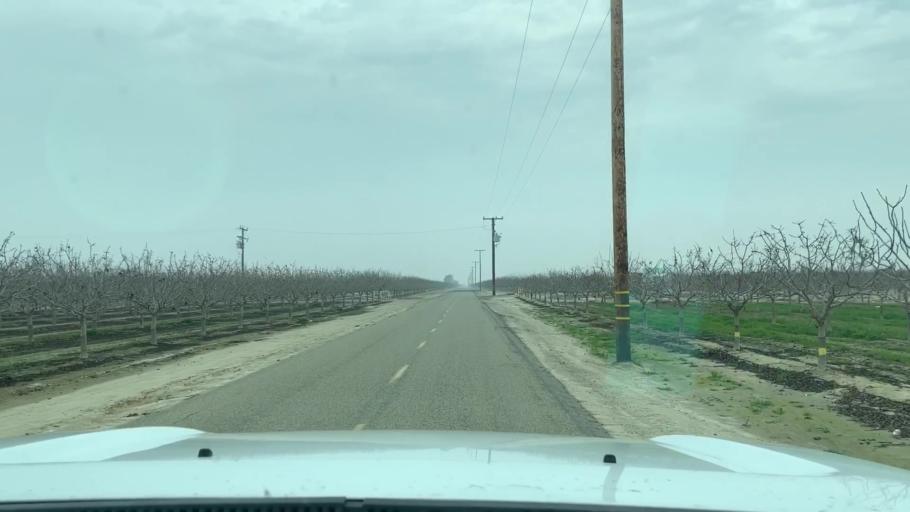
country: US
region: California
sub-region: Tulare County
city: Earlimart
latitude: 35.8193
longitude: -119.3408
